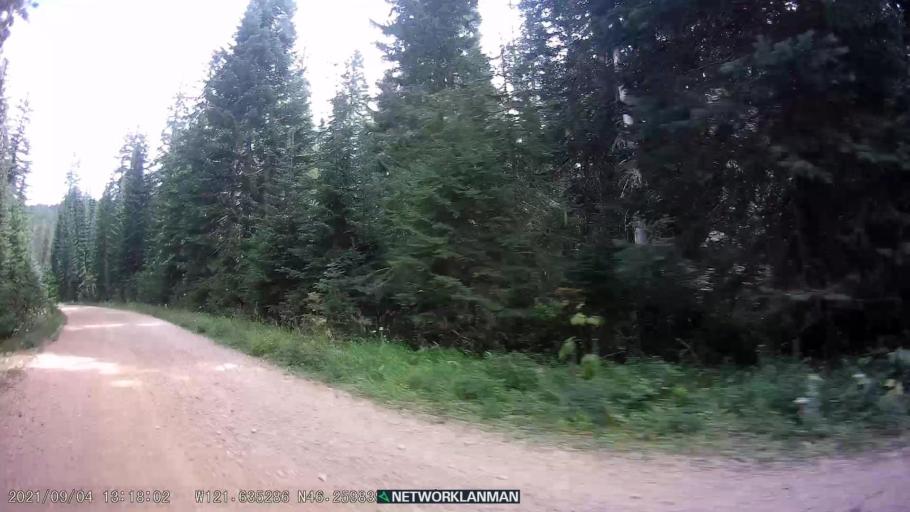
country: US
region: Washington
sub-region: Klickitat County
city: White Salmon
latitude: 46.2600
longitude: -121.6352
